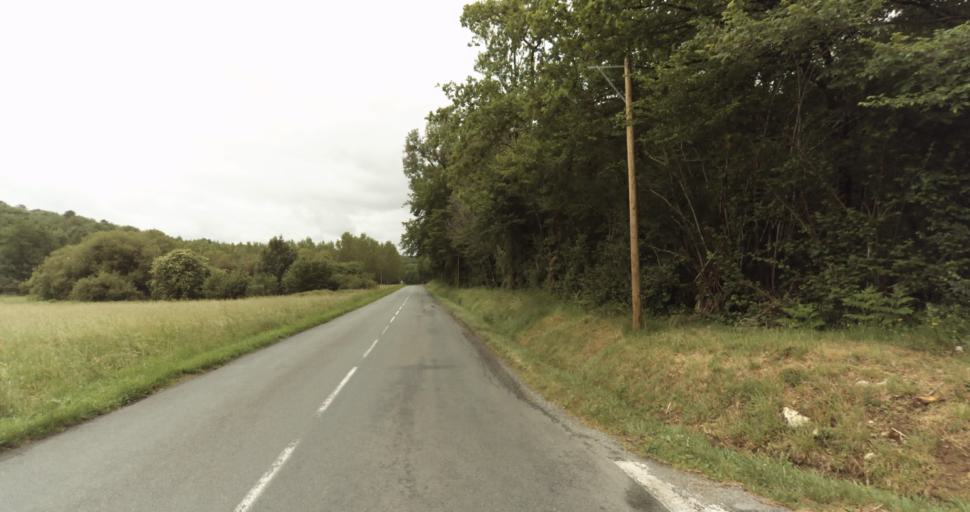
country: FR
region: Aquitaine
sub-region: Departement du Lot-et-Garonne
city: Villereal
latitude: 44.6666
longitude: 0.8778
